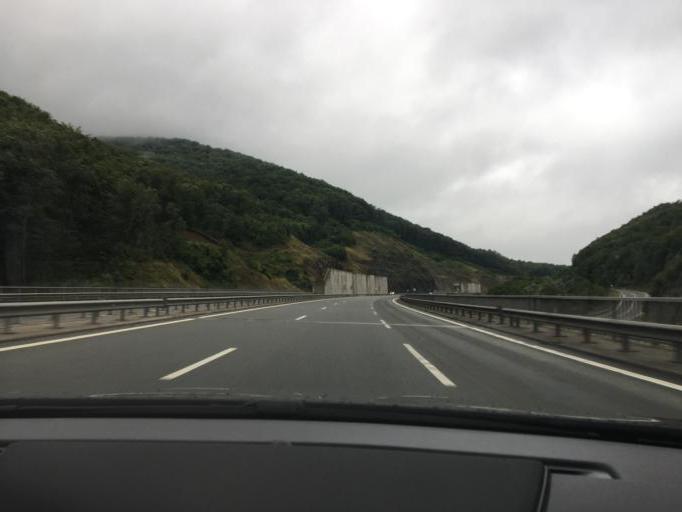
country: BG
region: Sofiya
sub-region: Obshtina Bozhurishte
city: Bozhurishte
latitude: 42.6691
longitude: 23.1499
